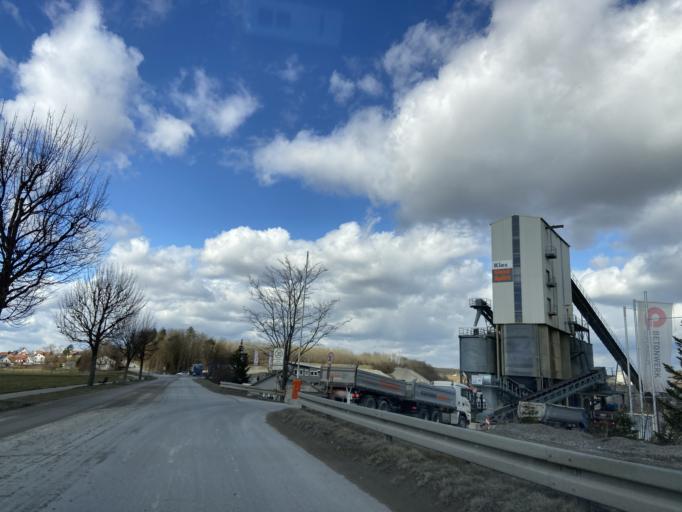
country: DE
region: Baden-Wuerttemberg
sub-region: Tuebingen Region
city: Ostrach
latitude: 47.9606
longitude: 9.3767
